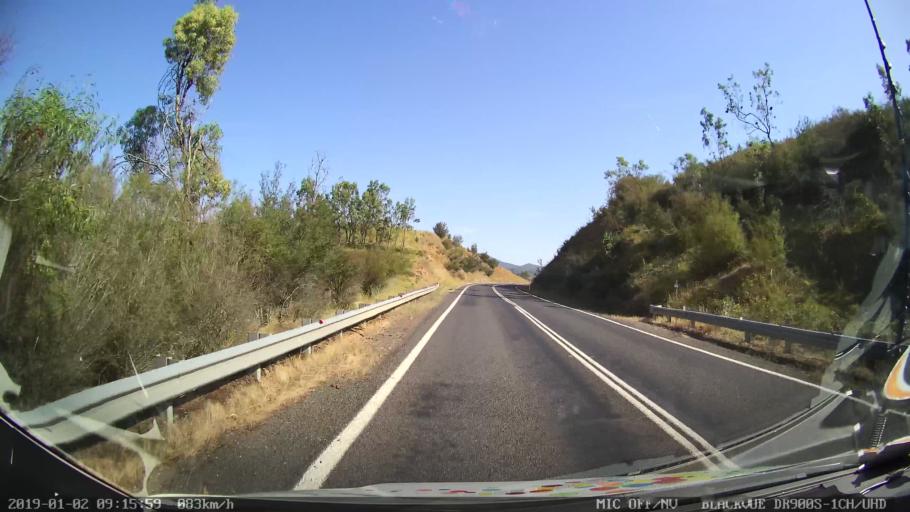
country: AU
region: New South Wales
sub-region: Tumut Shire
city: Tumut
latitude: -35.4586
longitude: 148.2819
